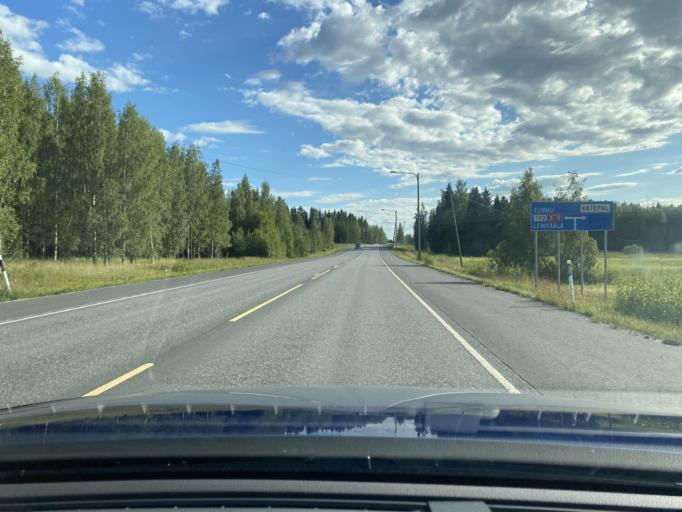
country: FI
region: Pirkanmaa
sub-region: Tampere
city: Lempaeaelae
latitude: 61.3287
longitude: 23.7755
